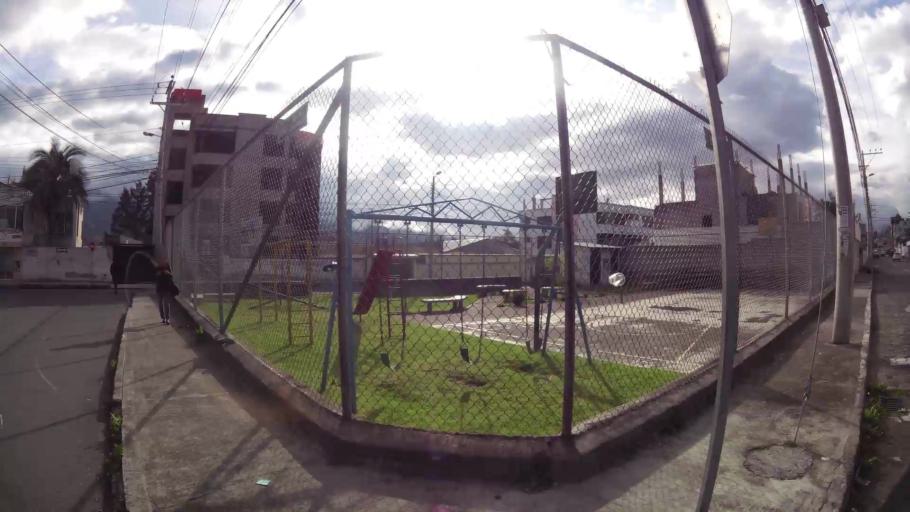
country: EC
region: Pichincha
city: Quito
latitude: -0.1345
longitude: -78.4676
